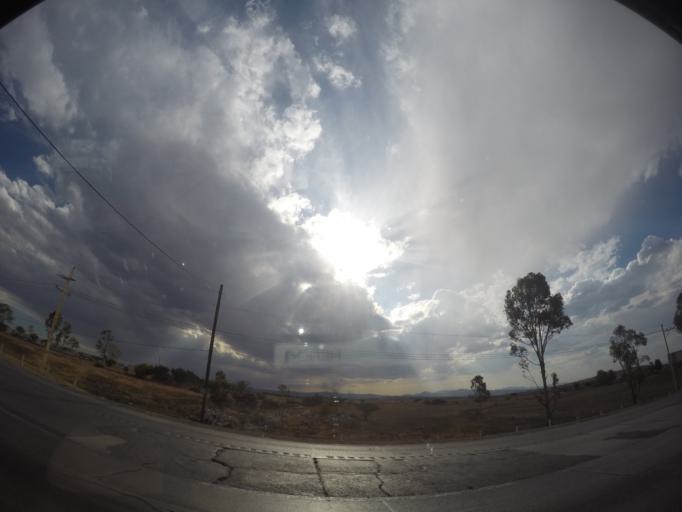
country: MX
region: Mexico
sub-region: Jilotepec
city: San Vicente (Calpulalpan Tercera Manzana)
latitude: 20.0693
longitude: -99.6036
